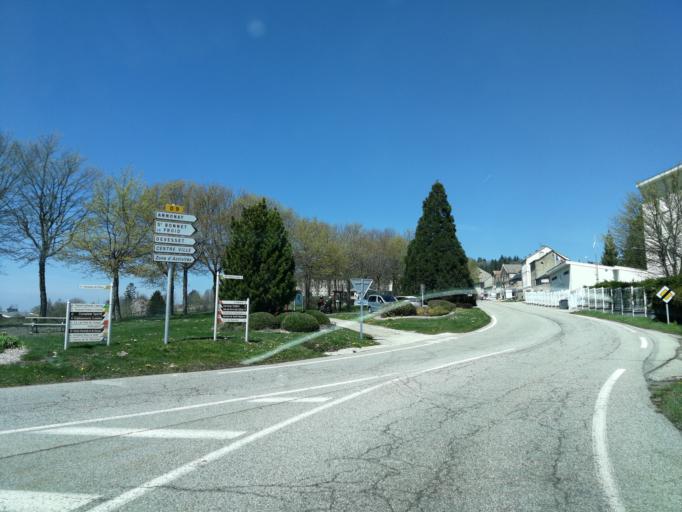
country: FR
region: Rhone-Alpes
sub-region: Departement de l'Ardeche
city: Saint-Agreve
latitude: 45.0064
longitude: 4.4024
